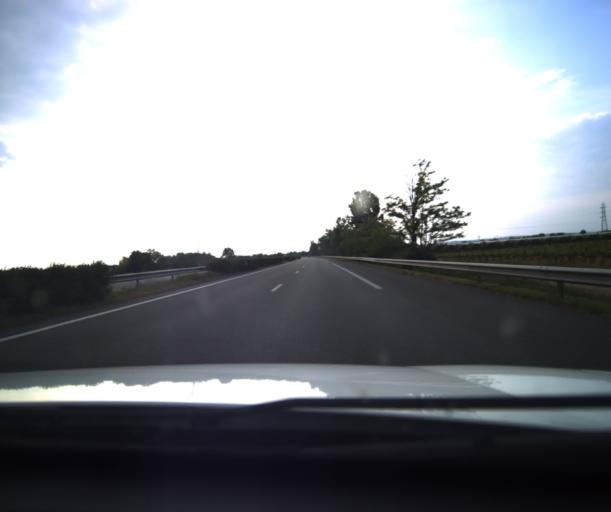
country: FR
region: Midi-Pyrenees
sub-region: Departement du Tarn-et-Garonne
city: Castelsarrasin
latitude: 44.0514
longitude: 1.1350
